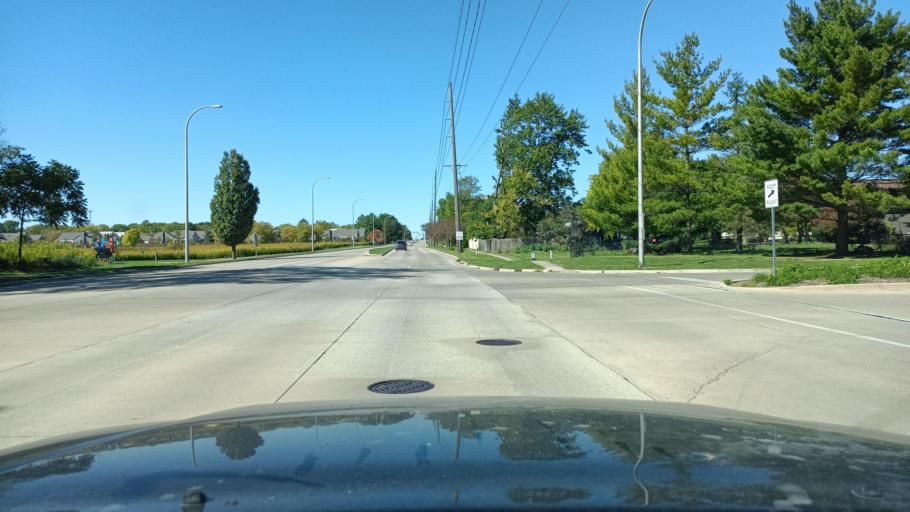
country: US
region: Illinois
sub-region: Champaign County
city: Urbana
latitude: 40.0839
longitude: -88.2013
